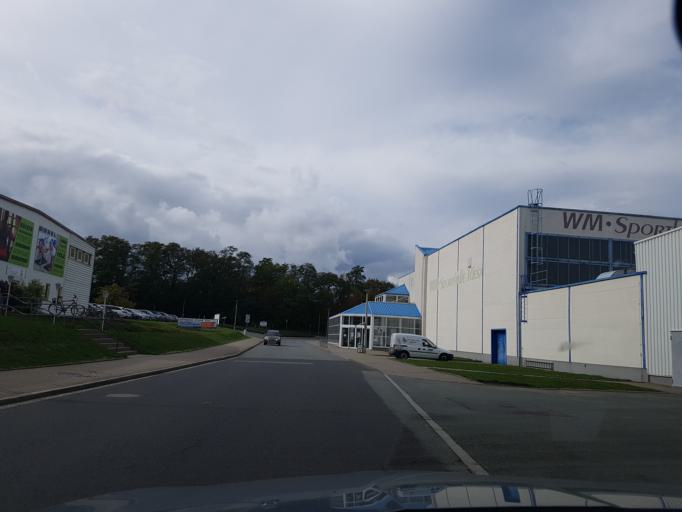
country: DE
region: Saxony
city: Riesa
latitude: 51.2971
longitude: 13.2942
